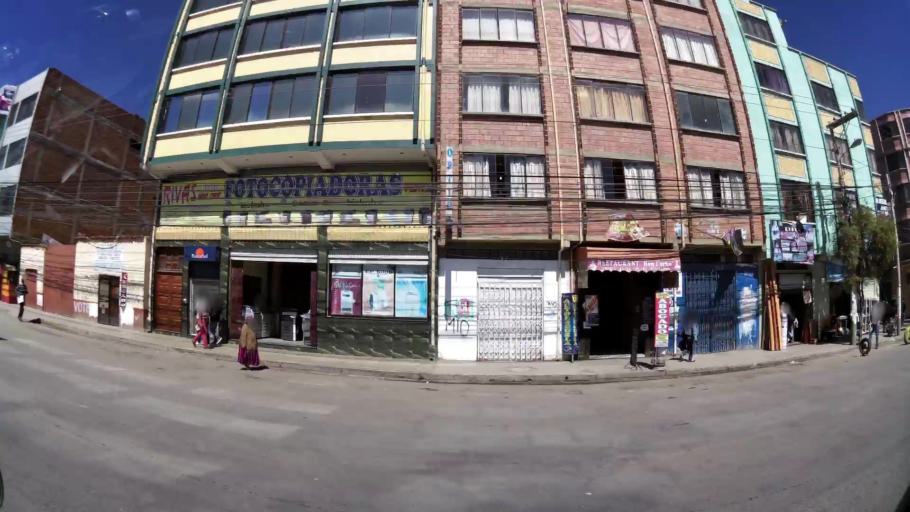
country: BO
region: La Paz
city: La Paz
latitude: -16.5025
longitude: -68.1656
